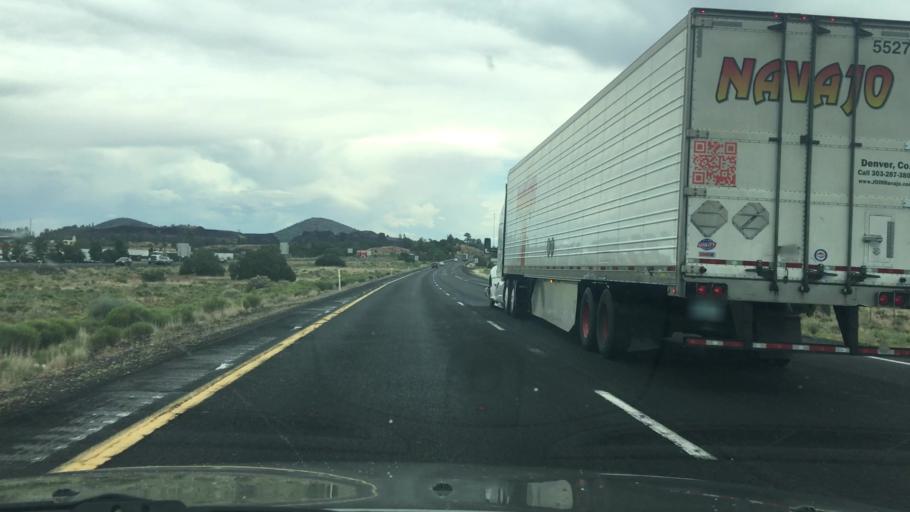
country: US
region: Arizona
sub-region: Coconino County
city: Flagstaff
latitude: 35.2179
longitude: -111.5739
